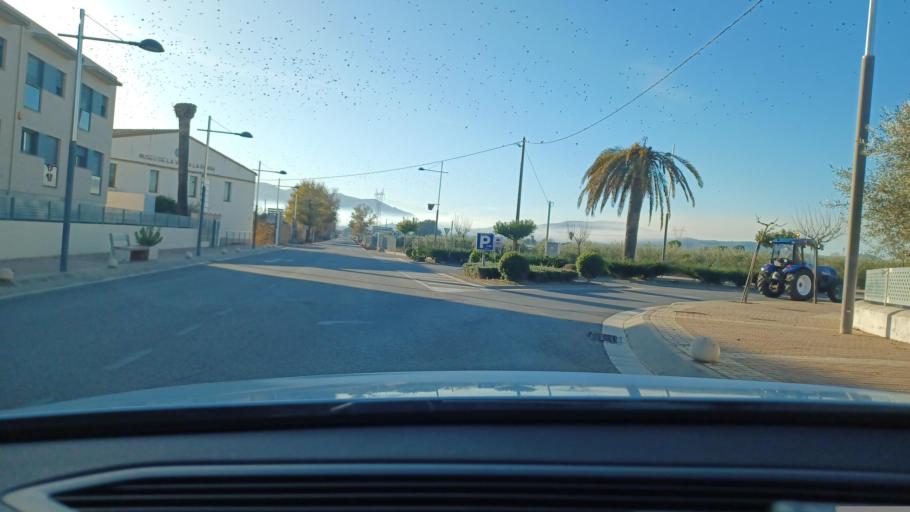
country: ES
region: Catalonia
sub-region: Provincia de Tarragona
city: Santa Barbara
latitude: 40.7126
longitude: 0.5018
